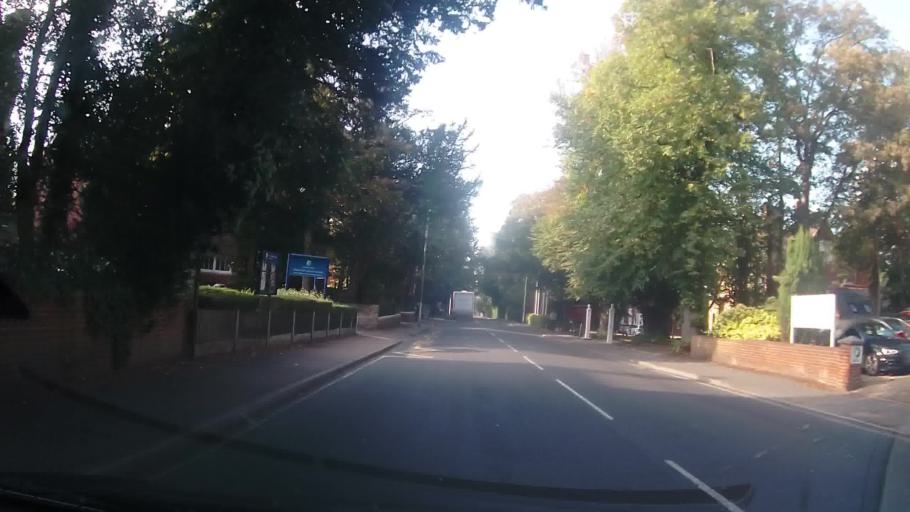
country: GB
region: England
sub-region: Kent
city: Canterbury
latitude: 51.2714
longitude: 1.0925
